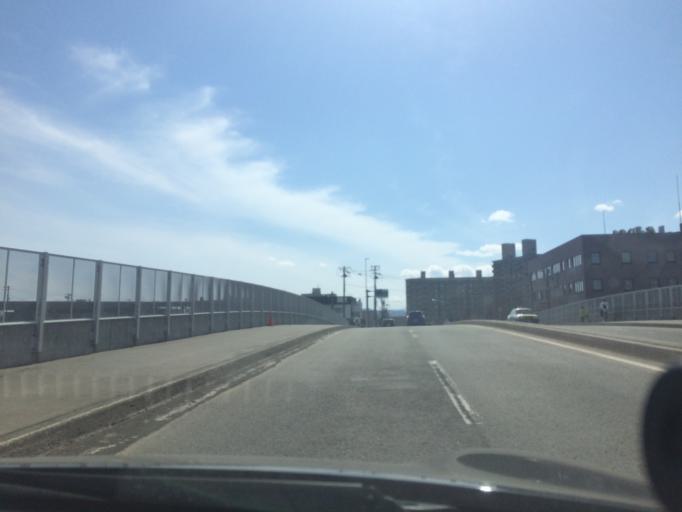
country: JP
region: Hokkaido
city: Sapporo
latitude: 43.0235
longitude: 141.4562
